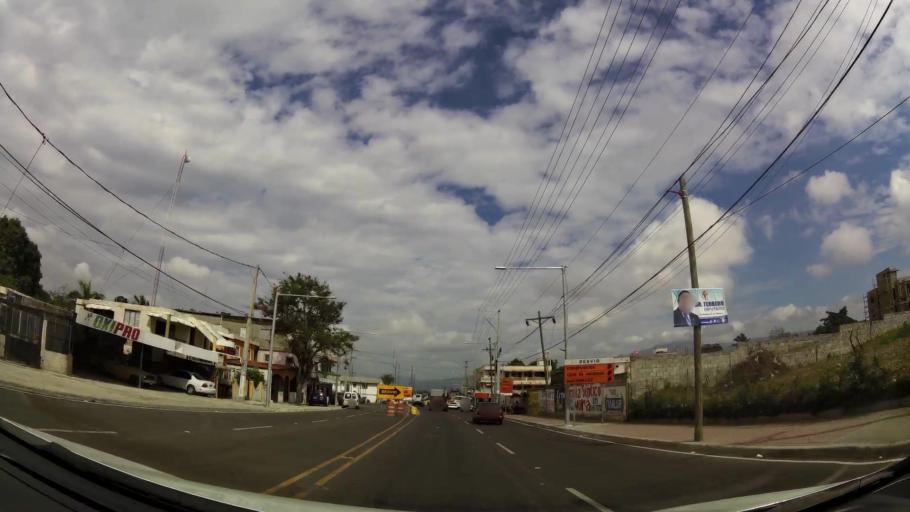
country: DO
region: Santiago
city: Santiago de los Caballeros
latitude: 19.4838
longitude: -70.7298
